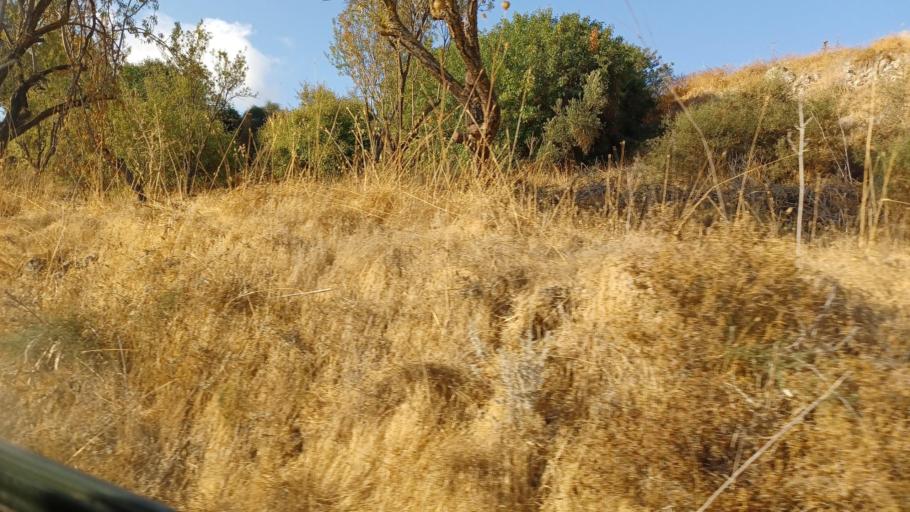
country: CY
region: Pafos
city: Tala
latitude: 34.9278
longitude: 32.4933
